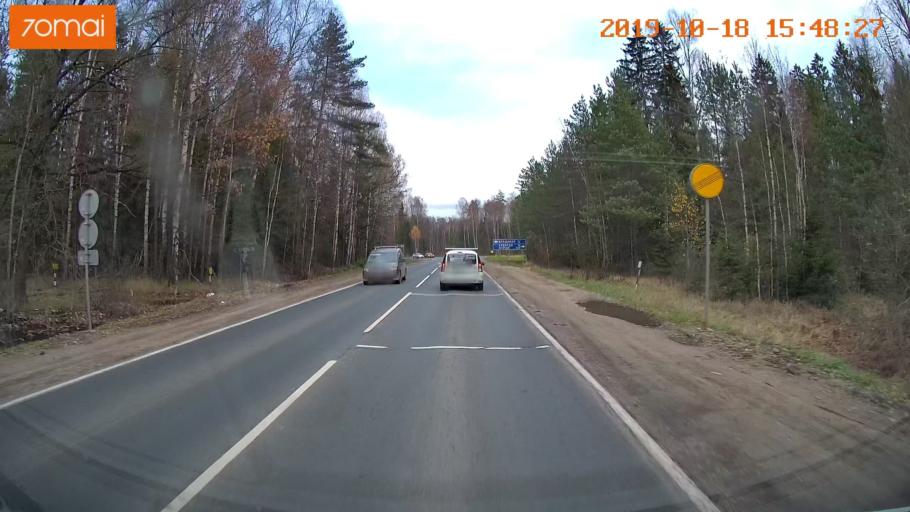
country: RU
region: Vladimir
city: Kommunar
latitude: 56.0177
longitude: 40.5801
